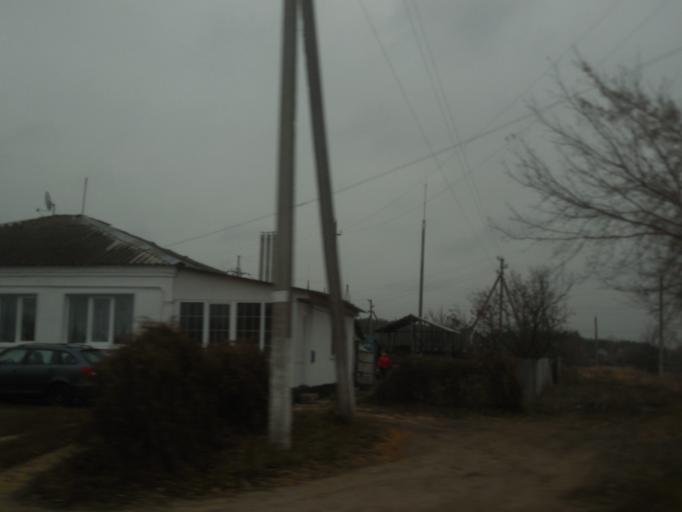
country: RU
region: Lipetsk
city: Zadonsk
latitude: 52.4806
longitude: 38.9658
